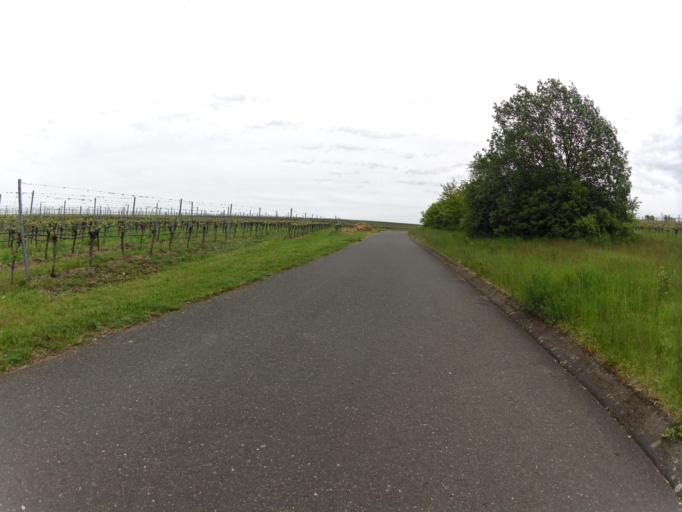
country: DE
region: Bavaria
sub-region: Regierungsbezirk Unterfranken
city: Nordheim
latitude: 49.8467
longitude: 10.1786
